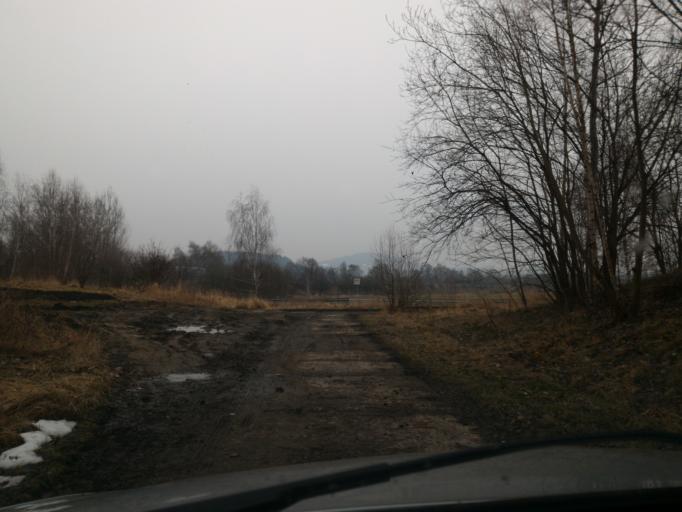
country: CZ
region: Ustecky
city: Varnsdorf
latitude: 50.9021
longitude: 14.6427
